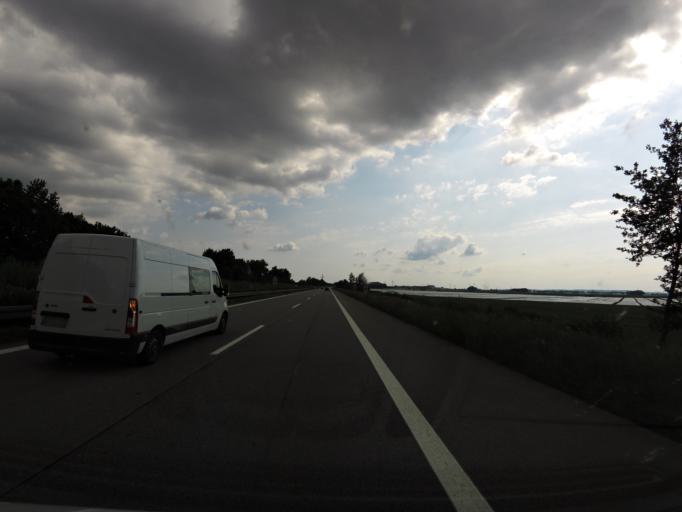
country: DE
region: Bavaria
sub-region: Lower Bavaria
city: Wallersdorf
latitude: 48.7595
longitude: 12.7693
